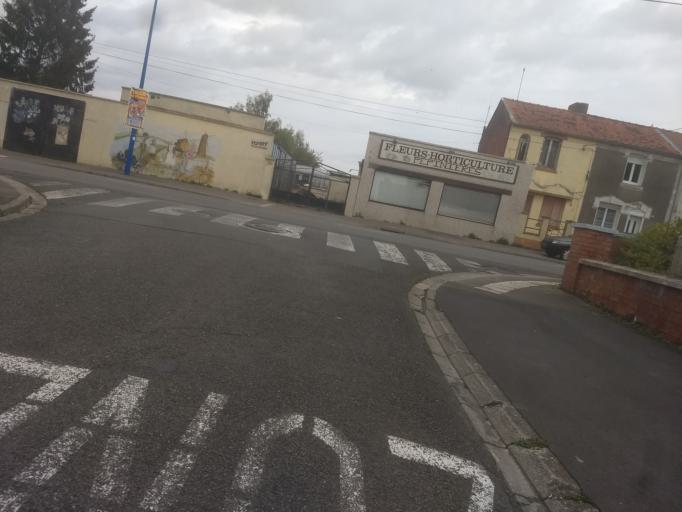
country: FR
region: Nord-Pas-de-Calais
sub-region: Departement du Pas-de-Calais
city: Beaurains
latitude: 50.2664
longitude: 2.7797
